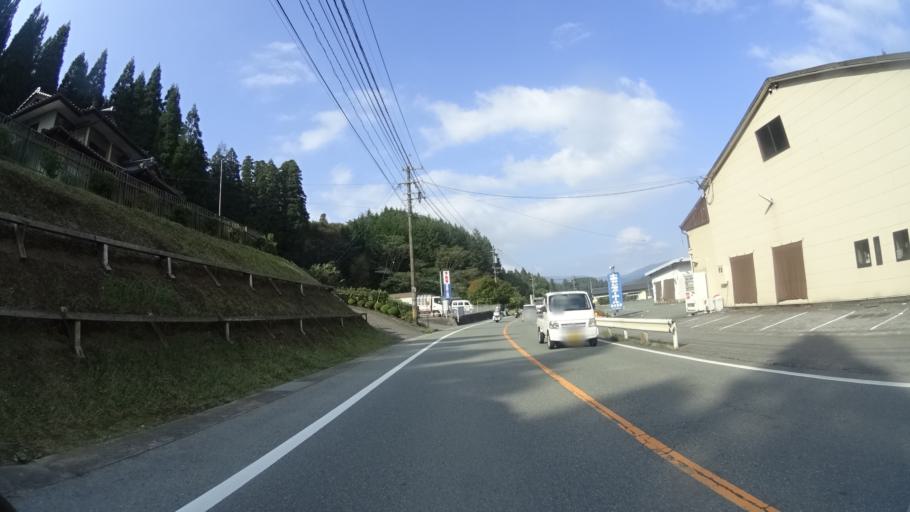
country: JP
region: Kumamoto
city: Aso
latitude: 33.1170
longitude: 131.0584
